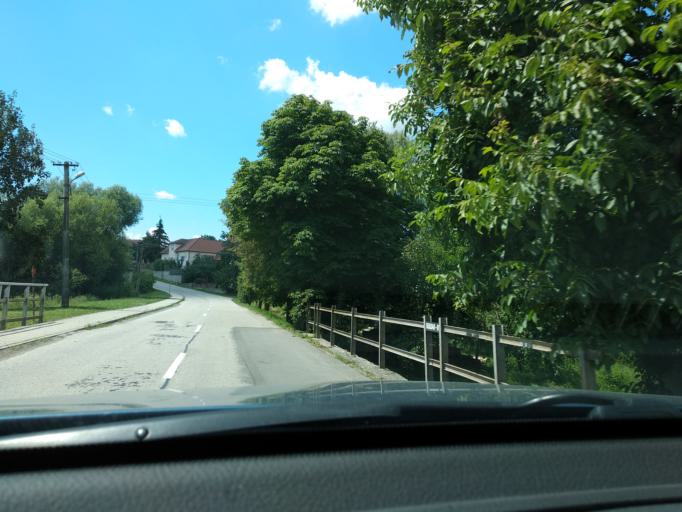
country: SK
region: Nitriansky
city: Banovce nad Bebravou
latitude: 48.7029
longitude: 18.1947
